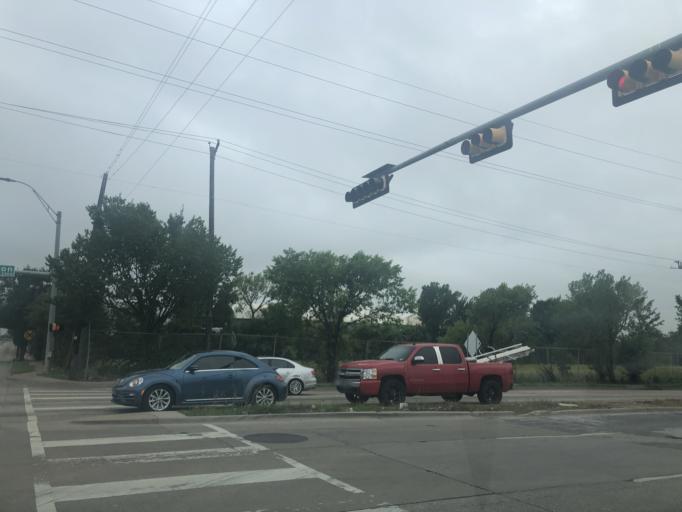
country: US
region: Texas
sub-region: Dallas County
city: Cockrell Hill
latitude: 32.7789
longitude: -96.8739
